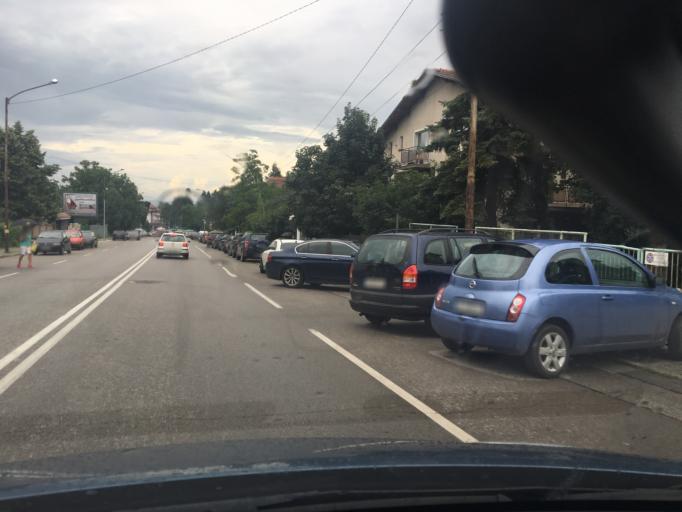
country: BG
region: Sofia-Capital
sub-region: Stolichna Obshtina
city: Sofia
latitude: 42.6569
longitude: 23.2651
